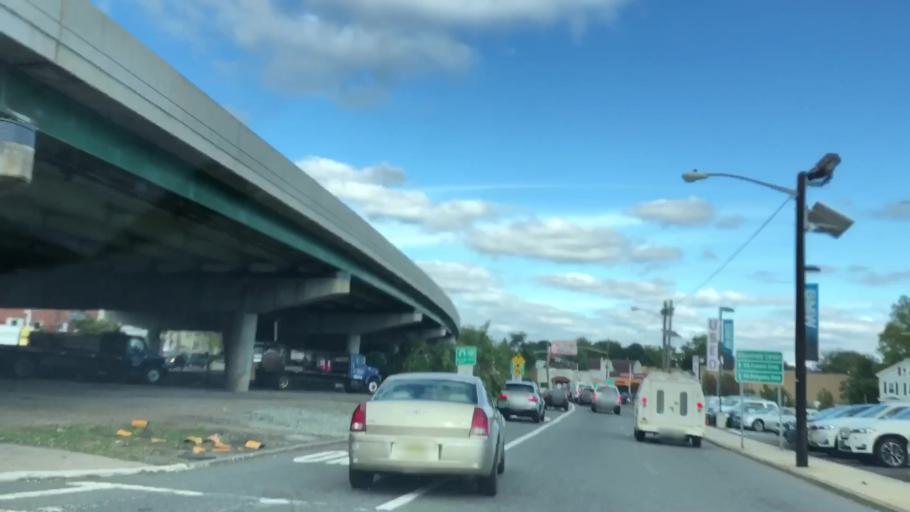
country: US
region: New Jersey
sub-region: Essex County
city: Glen Ridge
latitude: 40.7894
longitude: -74.1953
